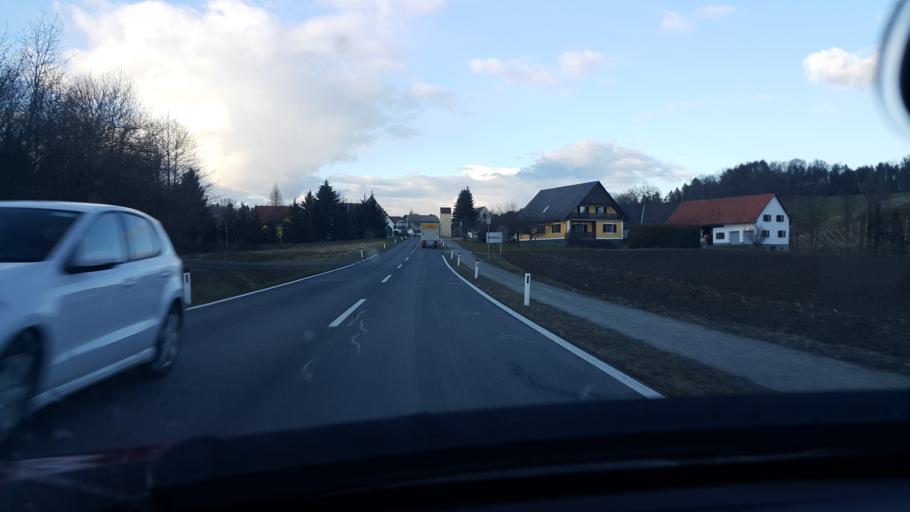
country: AT
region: Styria
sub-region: Politischer Bezirk Deutschlandsberg
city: Hollenegg
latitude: 46.7835
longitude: 15.2412
